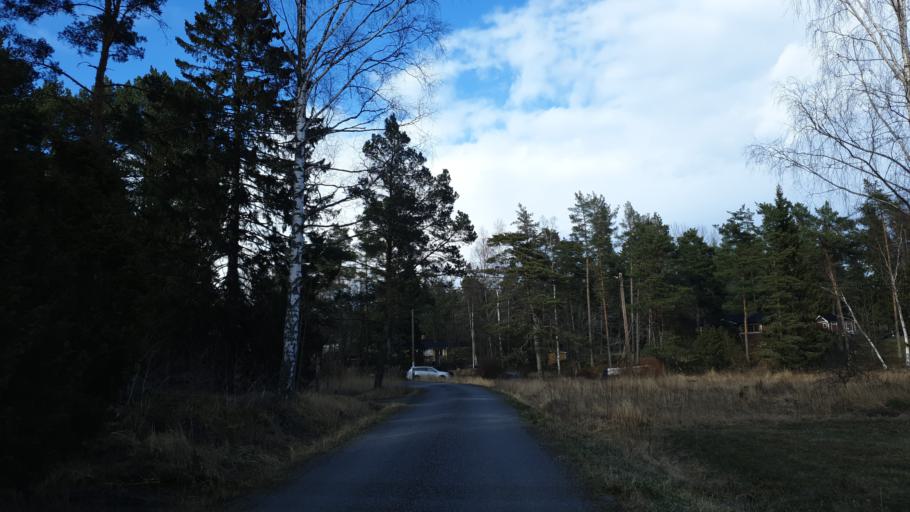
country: SE
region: Stockholm
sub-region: Varmdo Kommun
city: Holo
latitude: 59.2766
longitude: 18.6357
